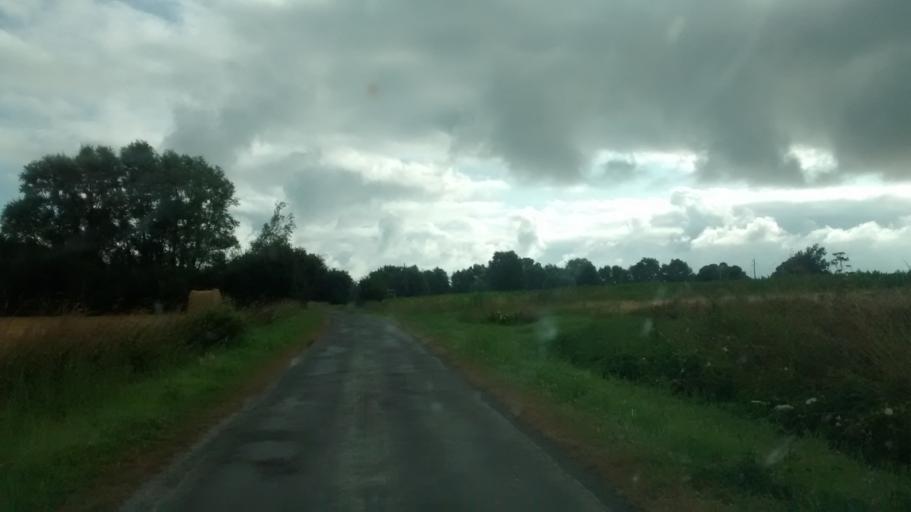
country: FR
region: Brittany
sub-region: Departement d'Ille-et-Vilaine
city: La Fresnais
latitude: 48.6086
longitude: -1.8610
